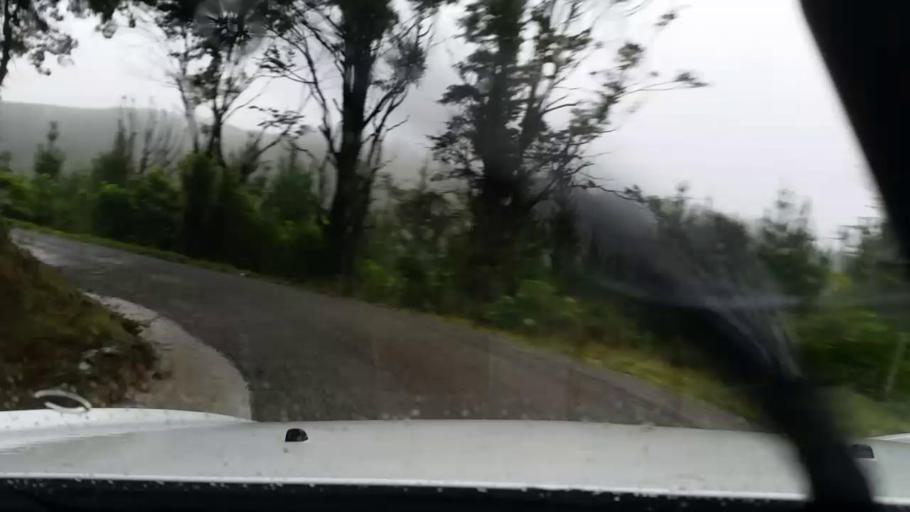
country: NZ
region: Wellington
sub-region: Masterton District
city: Masterton
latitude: -41.1867
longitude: 175.8191
